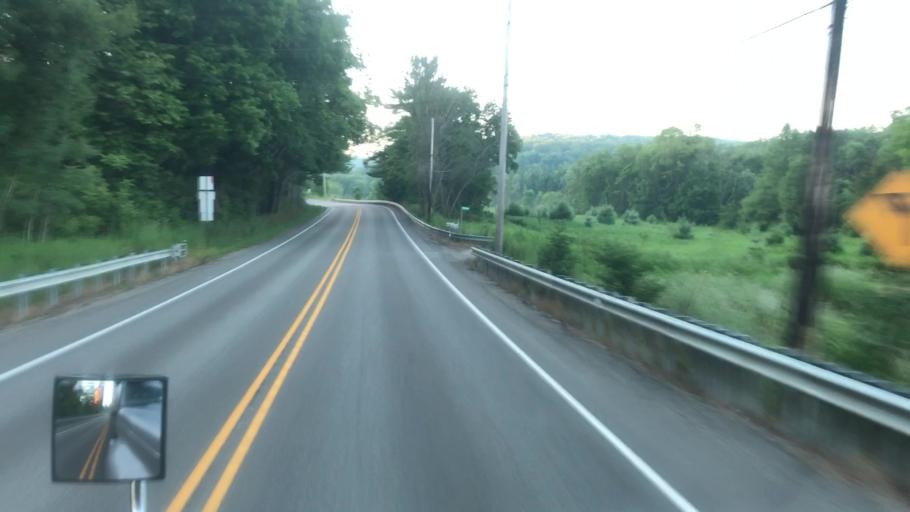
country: US
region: Pennsylvania
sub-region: Crawford County
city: Titusville
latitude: 41.6187
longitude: -79.6387
